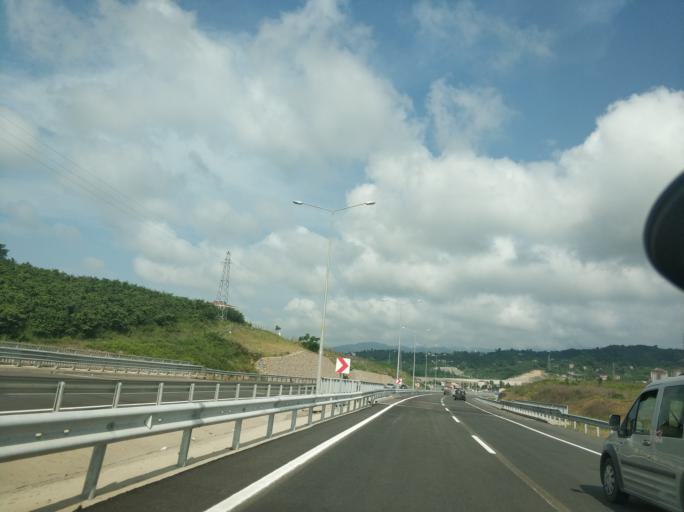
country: TR
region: Ordu
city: Ordu
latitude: 40.9562
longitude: 37.8878
